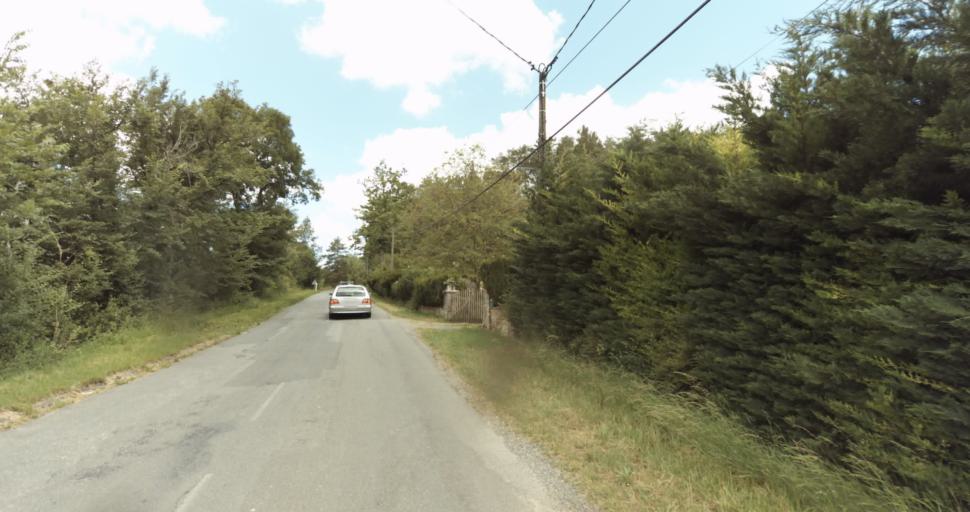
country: FR
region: Aquitaine
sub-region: Departement de la Dordogne
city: Beaumont-du-Perigord
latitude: 44.7617
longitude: 0.7629
